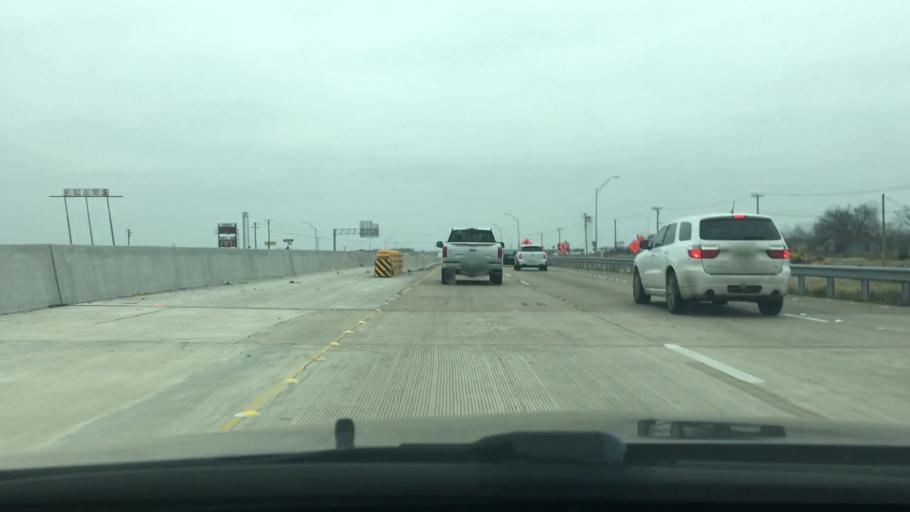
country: US
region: Texas
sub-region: Navarro County
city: Corsicana
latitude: 32.0597
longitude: -96.4520
